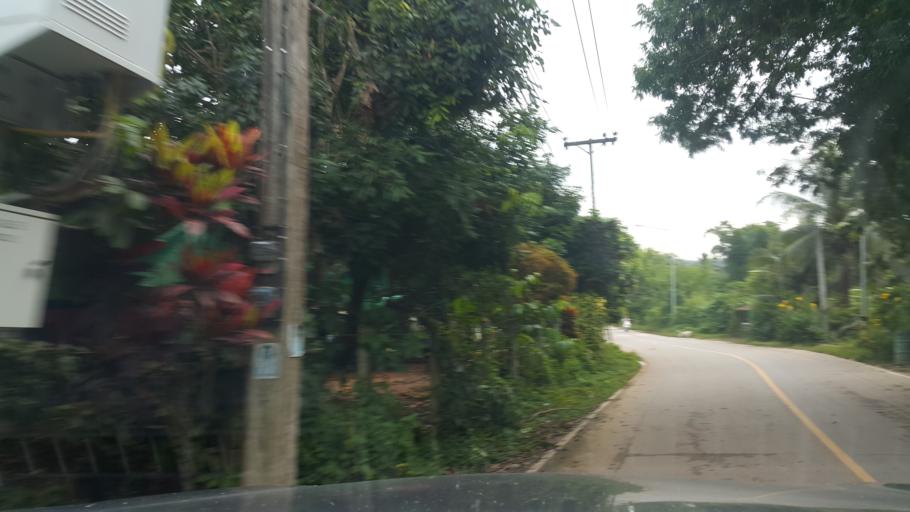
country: TH
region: Chiang Mai
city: San Sai
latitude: 18.9880
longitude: 99.1270
